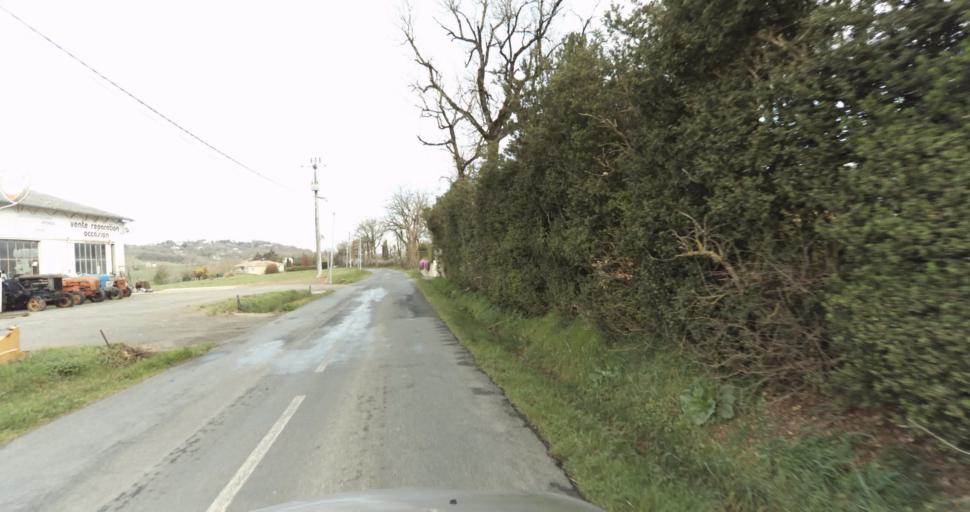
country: FR
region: Midi-Pyrenees
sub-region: Departement du Tarn
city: Puygouzon
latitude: 43.8900
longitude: 2.1926
